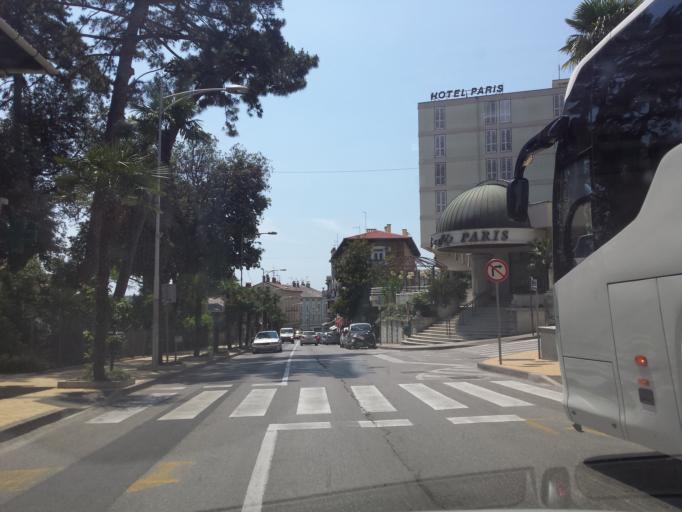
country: HR
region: Primorsko-Goranska
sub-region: Grad Opatija
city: Opatija
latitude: 45.3364
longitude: 14.3078
